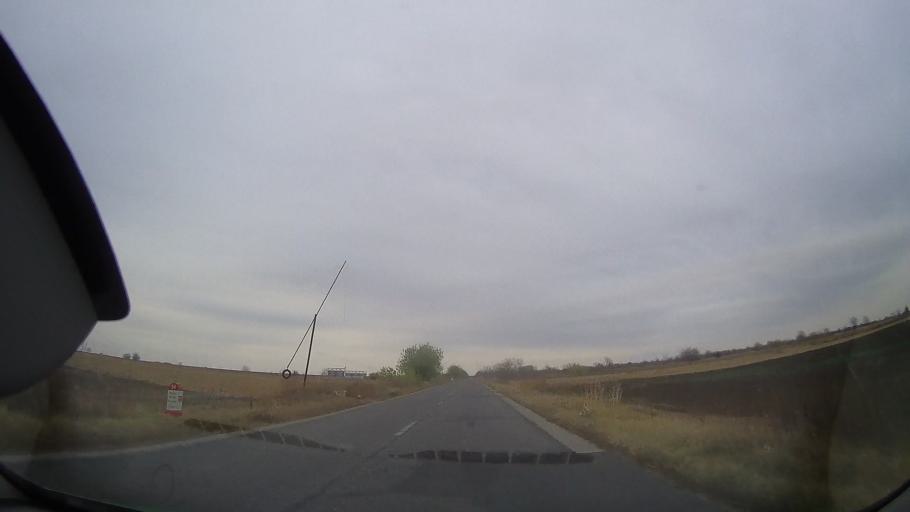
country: RO
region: Ialomita
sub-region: Comuna Milosesti
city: Milosesti
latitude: 44.7531
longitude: 27.2186
